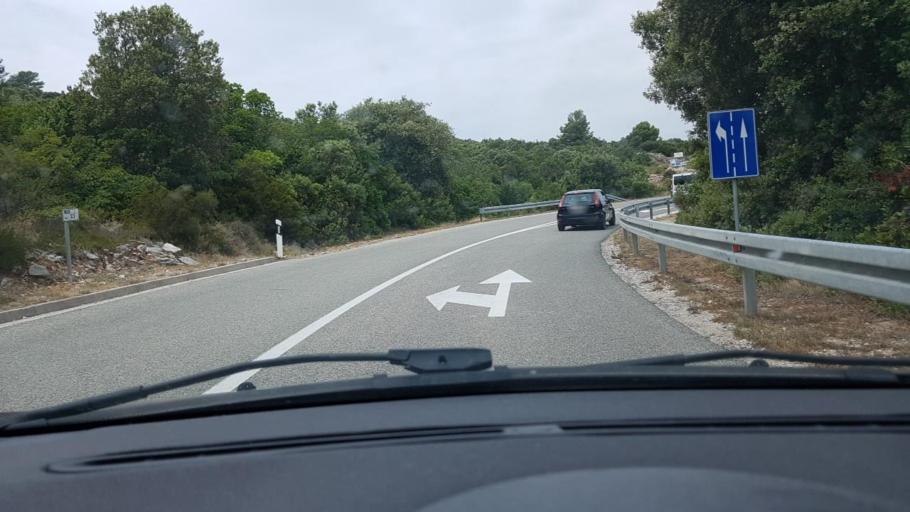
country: HR
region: Dubrovacko-Neretvanska
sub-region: Grad Korcula
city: Zrnovo
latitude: 42.9417
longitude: 17.0539
